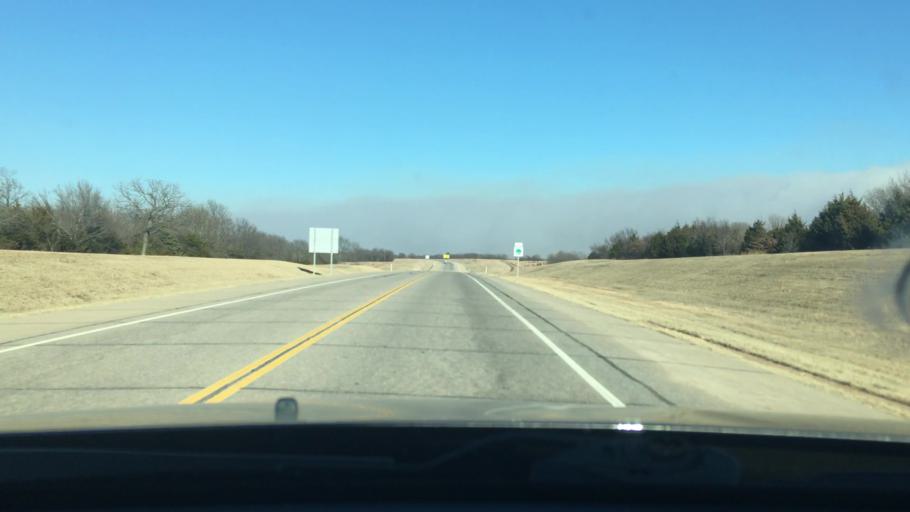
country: US
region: Oklahoma
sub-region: Murray County
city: Sulphur
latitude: 34.5469
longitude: -96.9529
